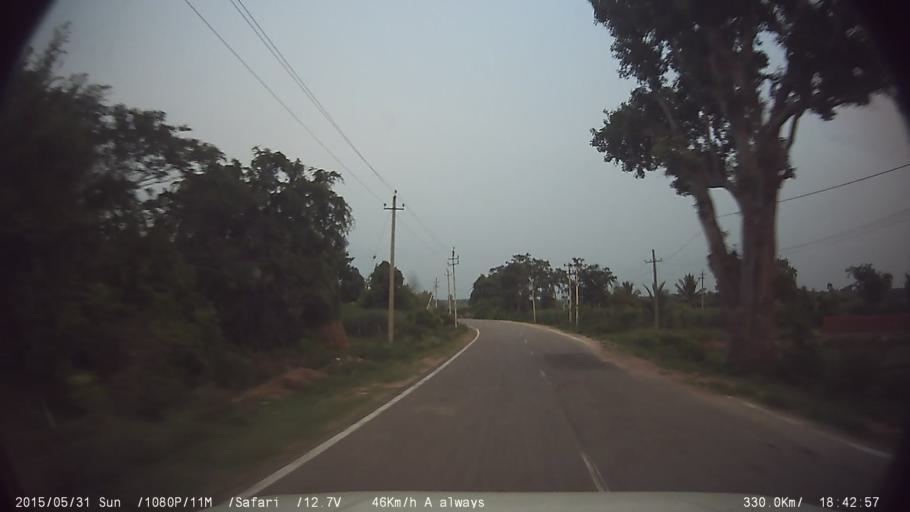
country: IN
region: Karnataka
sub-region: Mysore
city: Tirumakudal Narsipur
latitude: 12.1535
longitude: 76.8037
